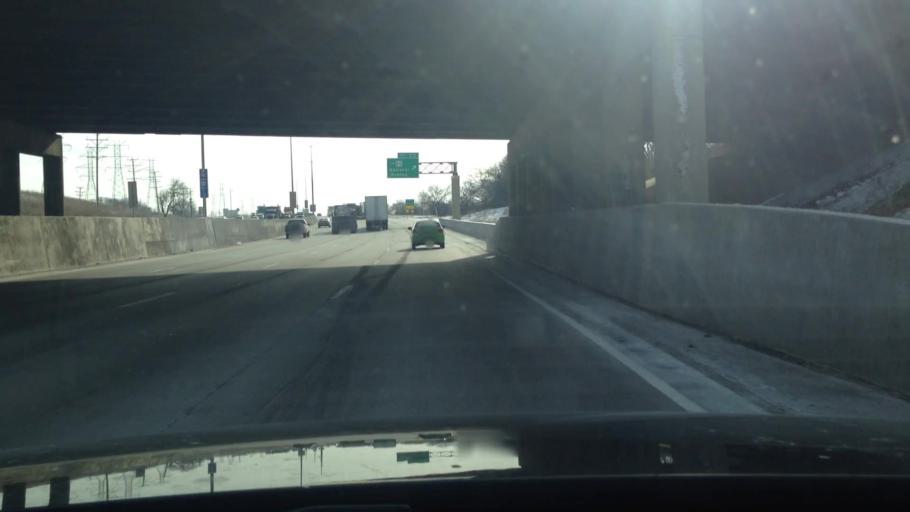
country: US
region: Wisconsin
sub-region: Milwaukee County
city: West Allis
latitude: 43.0028
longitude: -88.0385
